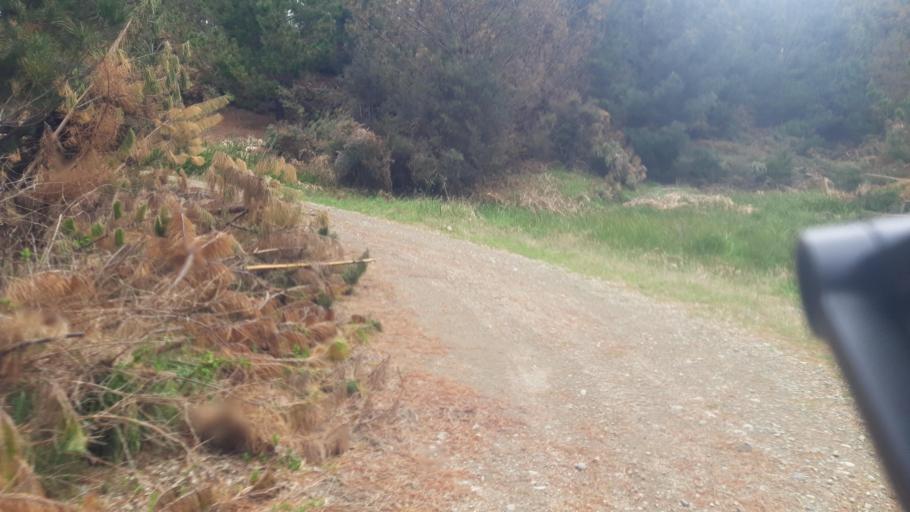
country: NZ
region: Tasman
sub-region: Tasman District
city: Wakefield
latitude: -41.7643
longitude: 172.8037
